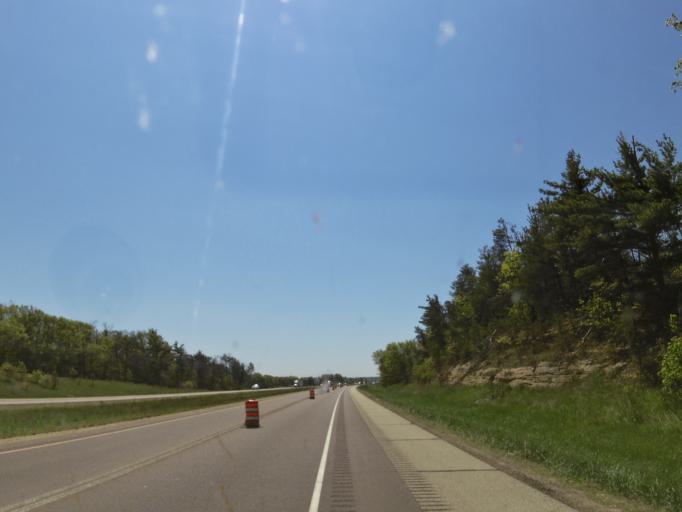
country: US
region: Wisconsin
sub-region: Monroe County
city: Tomah
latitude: 44.0811
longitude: -90.5258
